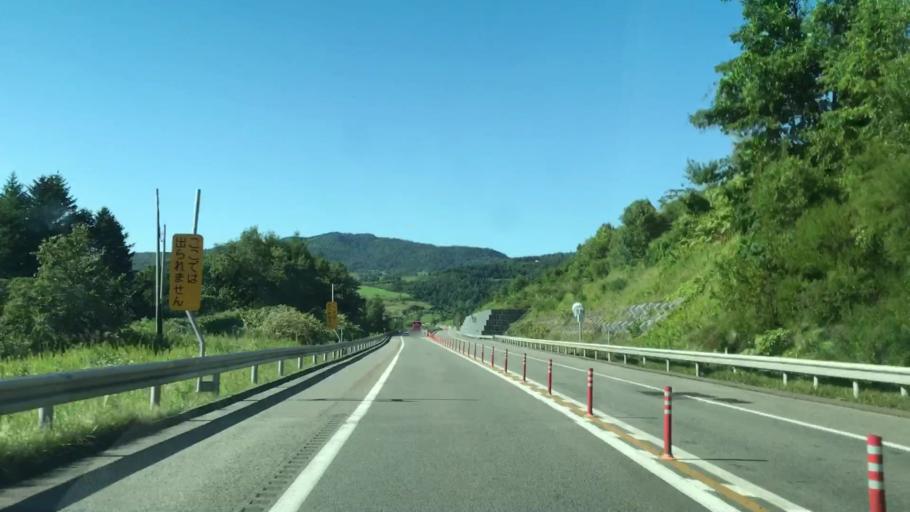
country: JP
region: Hokkaido
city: Date
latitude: 42.5405
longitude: 140.7954
